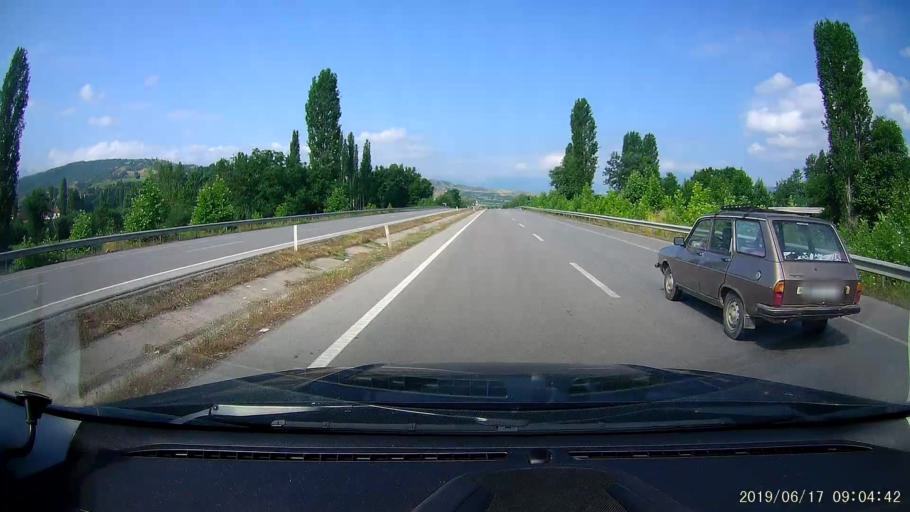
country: TR
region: Amasya
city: Tasova
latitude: 40.7431
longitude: 36.2824
